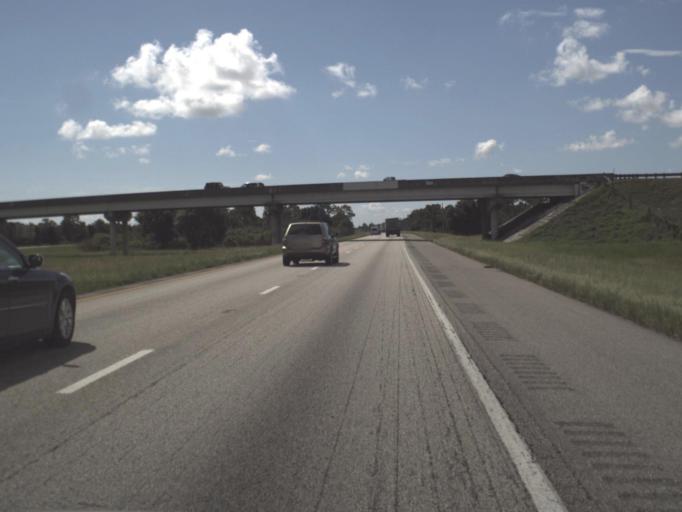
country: US
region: Florida
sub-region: Charlotte County
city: Harbour Heights
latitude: 27.0037
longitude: -82.0386
